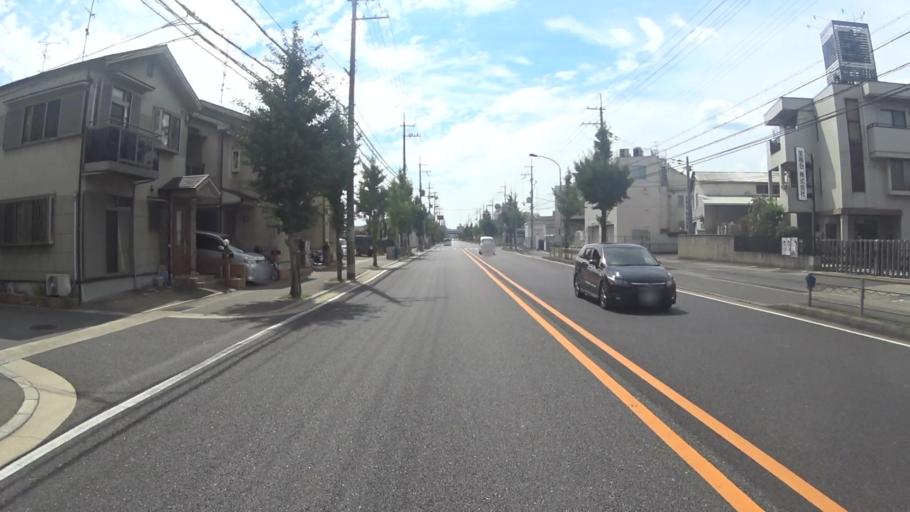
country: JP
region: Kyoto
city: Muko
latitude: 34.9181
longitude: 135.7296
